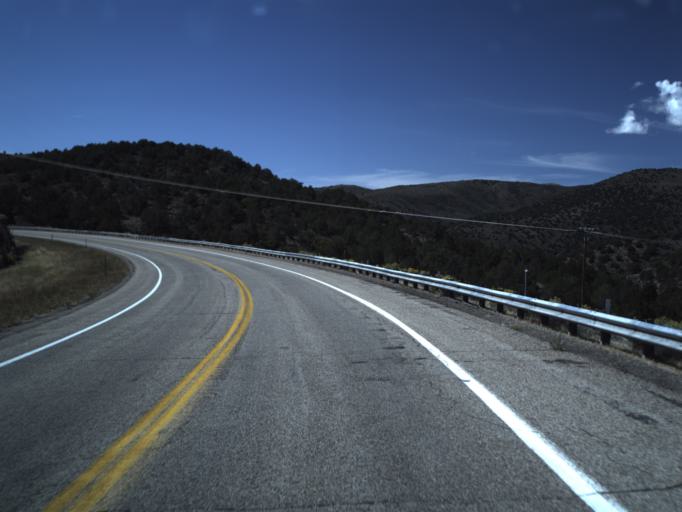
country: US
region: Utah
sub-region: Washington County
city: Enterprise
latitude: 37.4680
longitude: -113.6333
